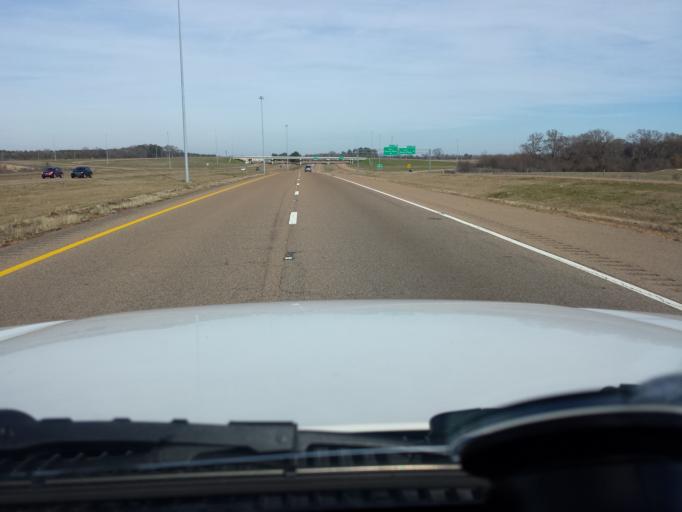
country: US
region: Mississippi
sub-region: Madison County
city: Canton
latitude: 32.5794
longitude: -90.0720
